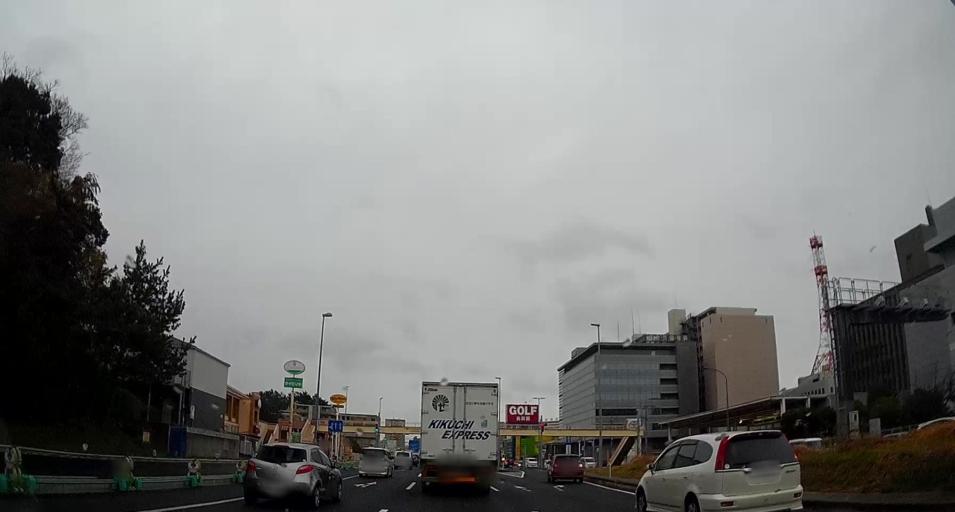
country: JP
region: Chiba
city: Chiba
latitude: 35.6182
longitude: 140.0985
